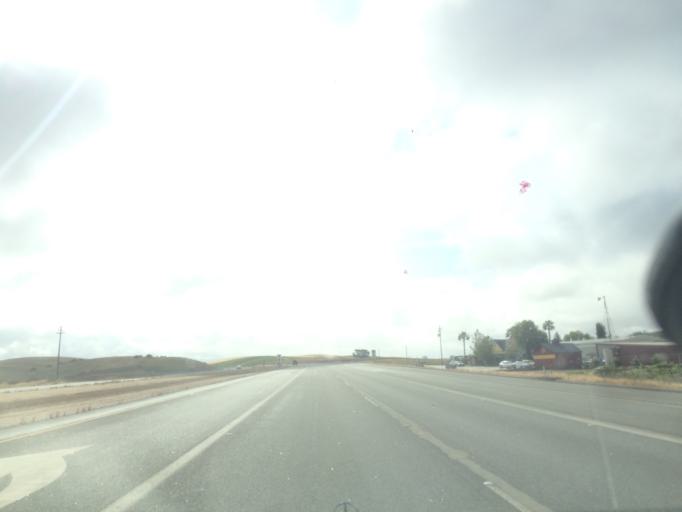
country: US
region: California
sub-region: San Luis Obispo County
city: Paso Robles
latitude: 35.6561
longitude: -120.5365
